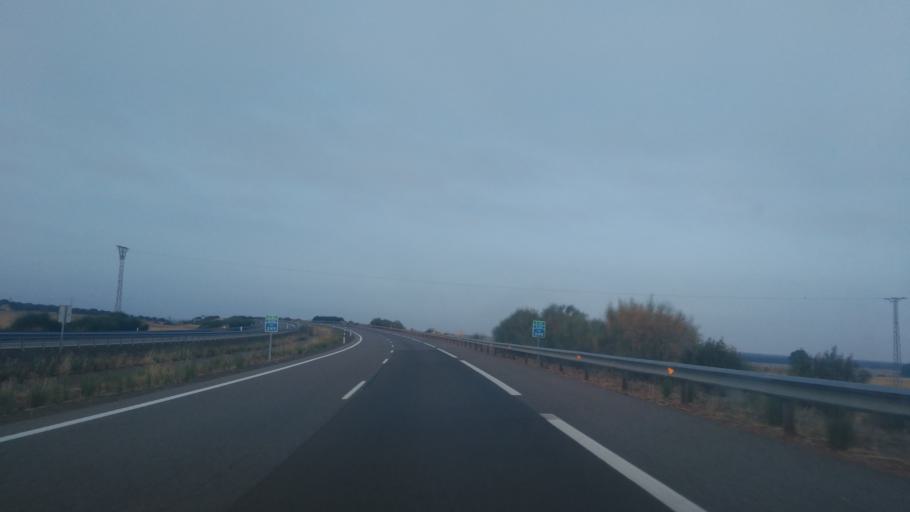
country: ES
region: Castille and Leon
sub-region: Provincia de Salamanca
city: Doninos de Salamanca
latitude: 40.9465
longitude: -5.7659
